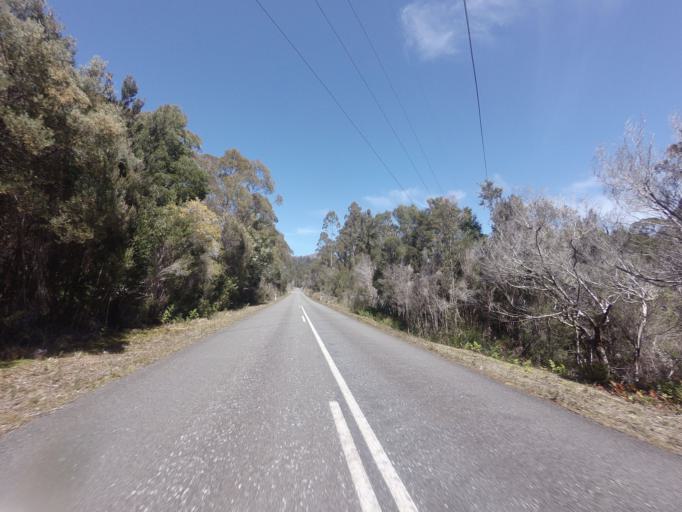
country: AU
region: Tasmania
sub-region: Huon Valley
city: Geeveston
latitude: -42.8322
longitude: 146.2685
